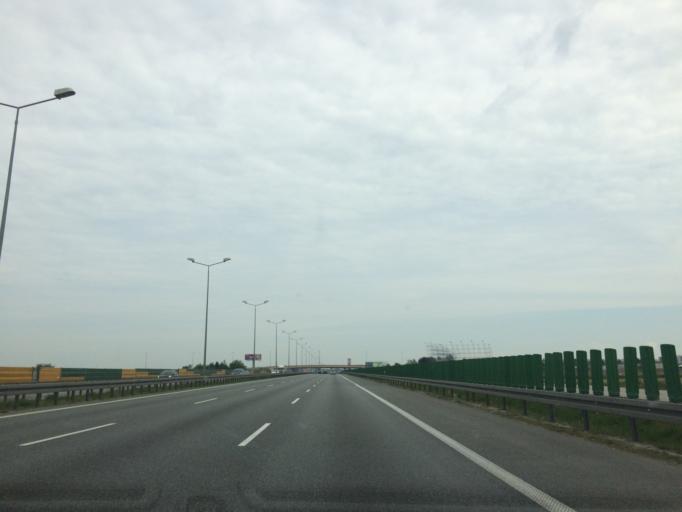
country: PL
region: Masovian Voivodeship
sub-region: Warszawa
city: Ursus
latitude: 52.2244
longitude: 20.8730
